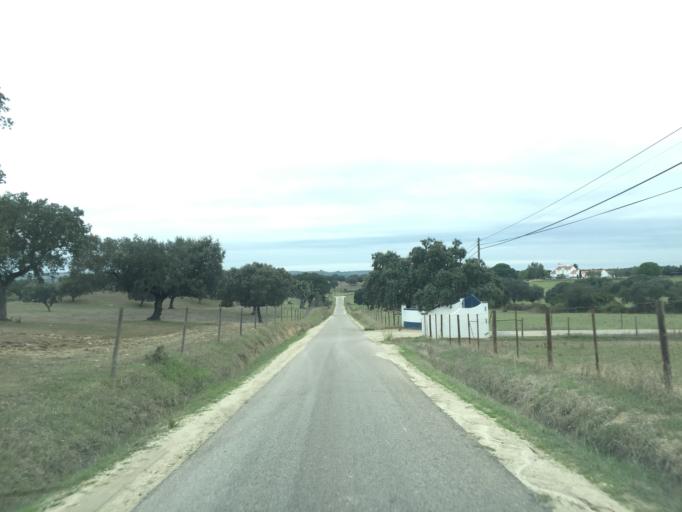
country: PT
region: Portalegre
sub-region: Fronteira
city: Vale da Amoreira
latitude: 39.0511
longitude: -7.7752
